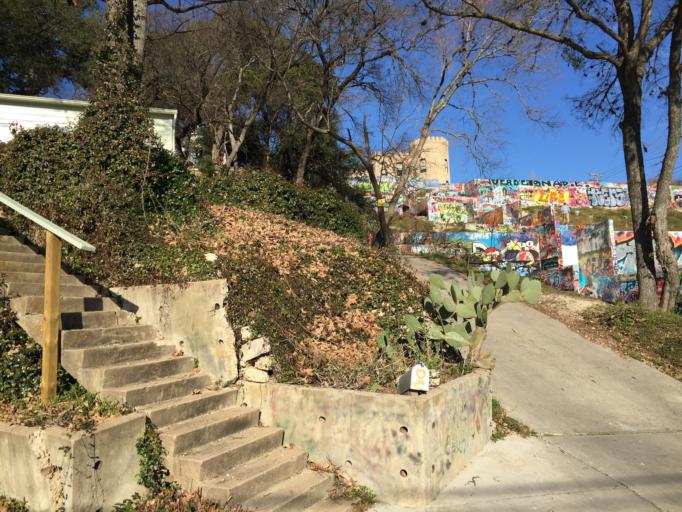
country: US
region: Texas
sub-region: Travis County
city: Austin
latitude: 30.2758
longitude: -97.7531
